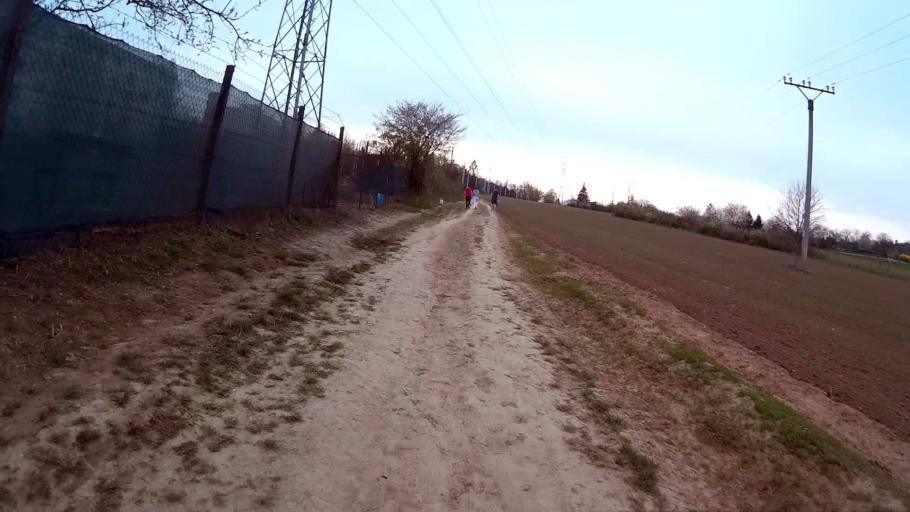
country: CZ
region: South Moravian
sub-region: Mesto Brno
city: Mokra Hora
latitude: 49.2268
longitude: 16.5564
